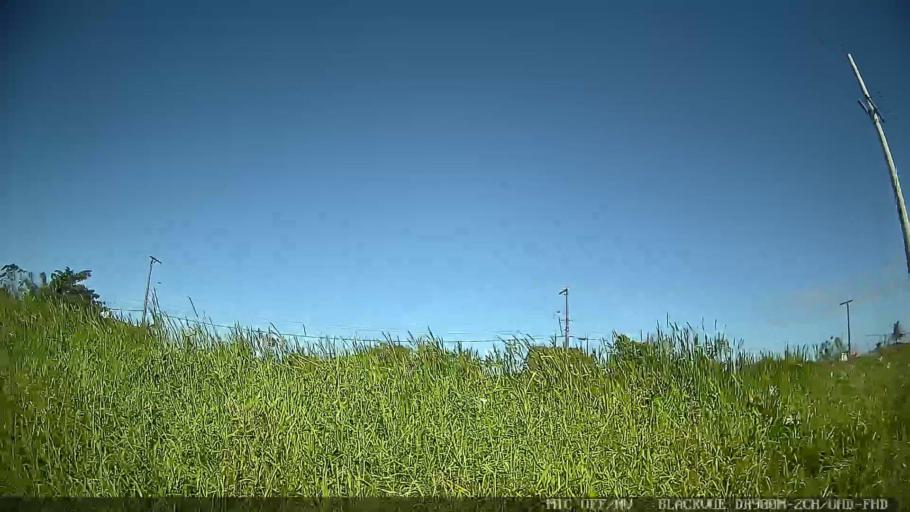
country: BR
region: Sao Paulo
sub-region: Itanhaem
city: Itanhaem
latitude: -24.2216
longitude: -46.8658
